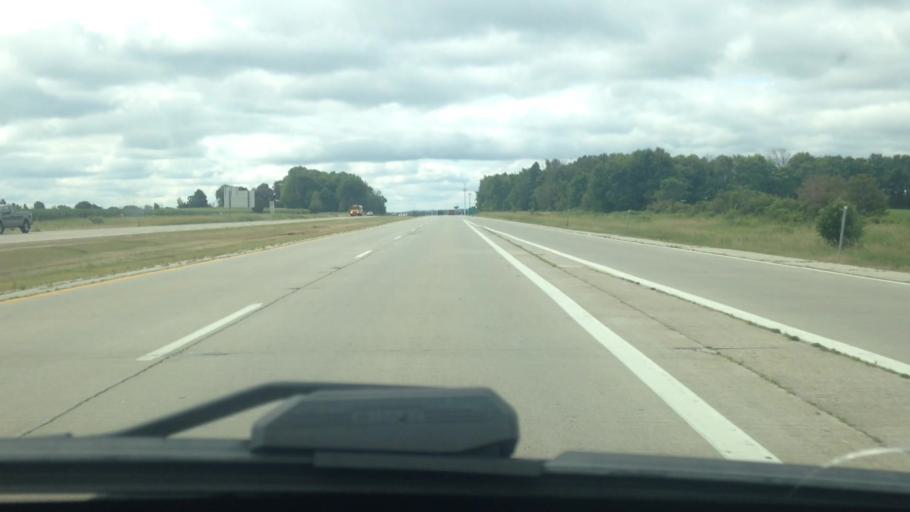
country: US
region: Wisconsin
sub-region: Washington County
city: Jackson
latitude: 43.3497
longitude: -88.1911
